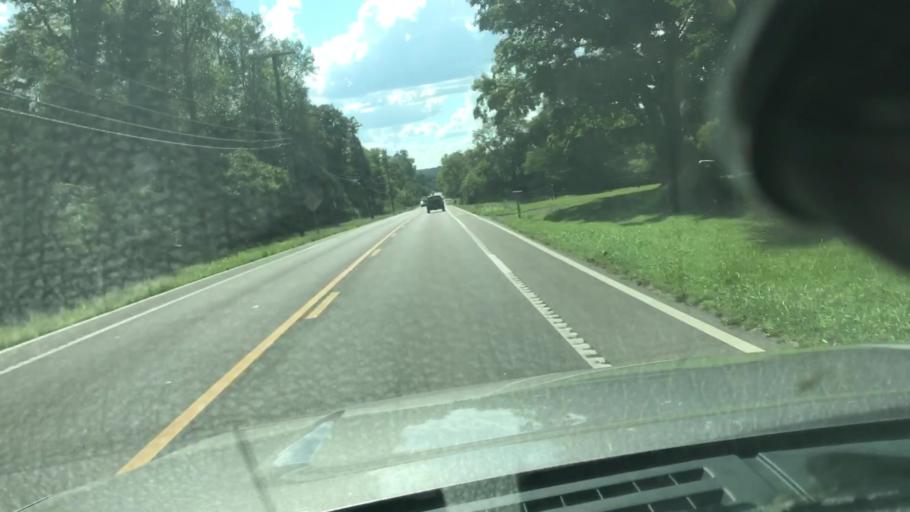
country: US
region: Tennessee
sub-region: Cheatham County
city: Pegram
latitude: 36.0300
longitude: -86.9980
